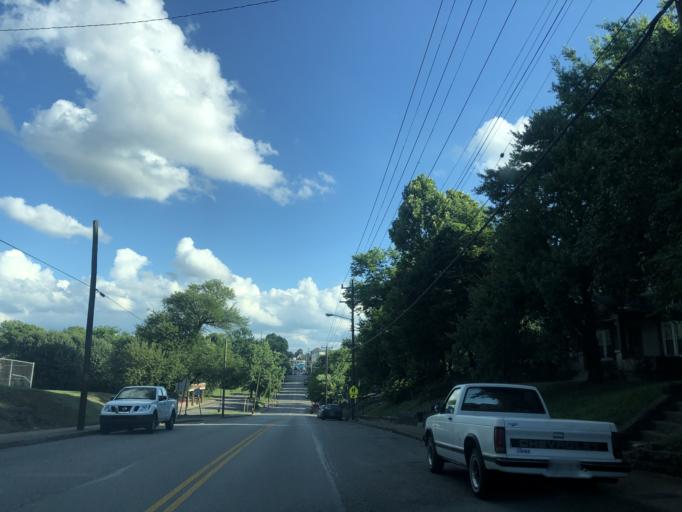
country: US
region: Tennessee
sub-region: Davidson County
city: Nashville
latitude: 36.1811
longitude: -86.7549
